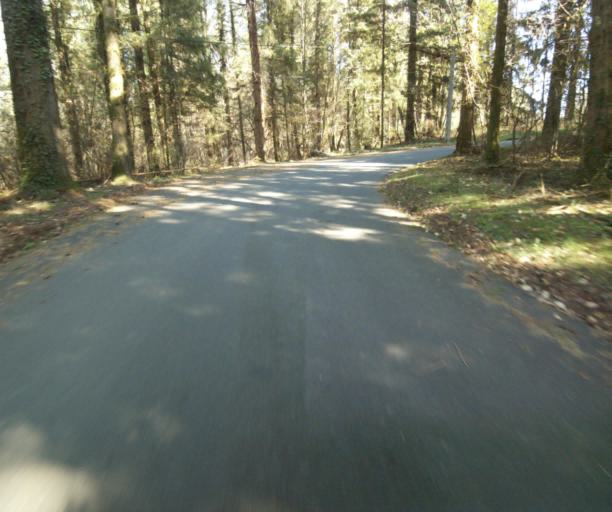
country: FR
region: Limousin
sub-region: Departement de la Correze
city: Tulle
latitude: 45.2824
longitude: 1.7240
